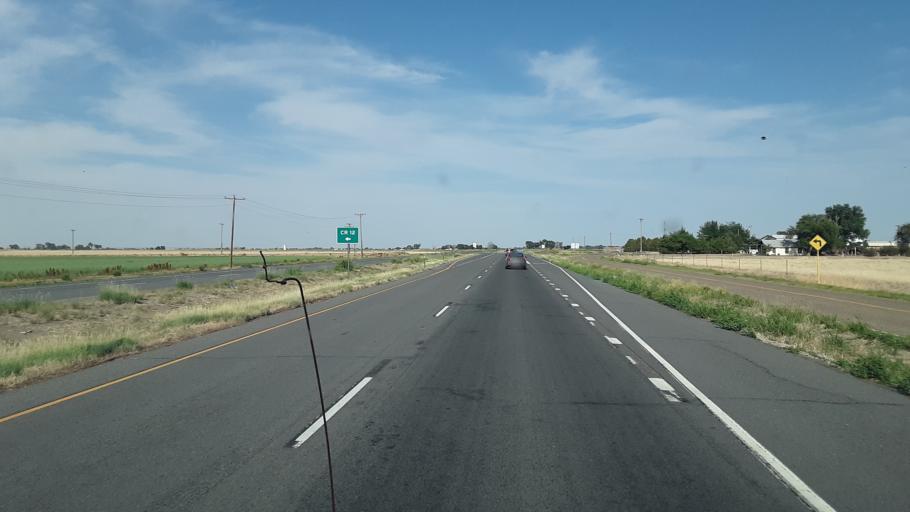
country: US
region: Colorado
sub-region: Bent County
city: Las Animas
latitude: 38.0881
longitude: -103.2005
